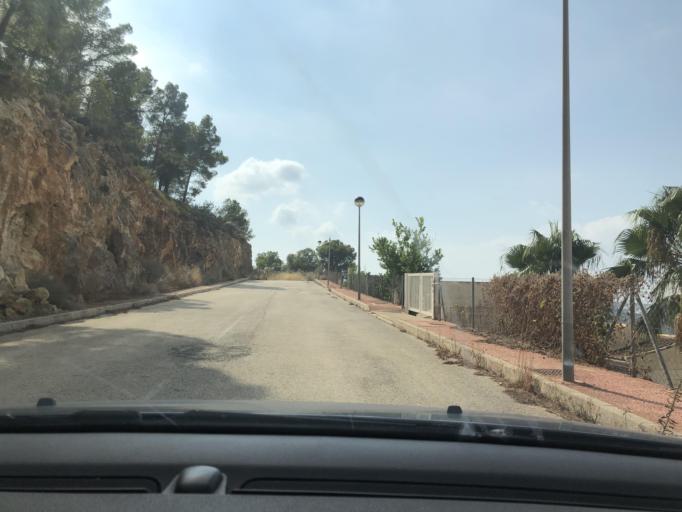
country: ES
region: Valencia
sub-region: Provincia de Alicante
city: Callosa d'En Sarria
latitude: 38.6345
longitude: -0.1119
